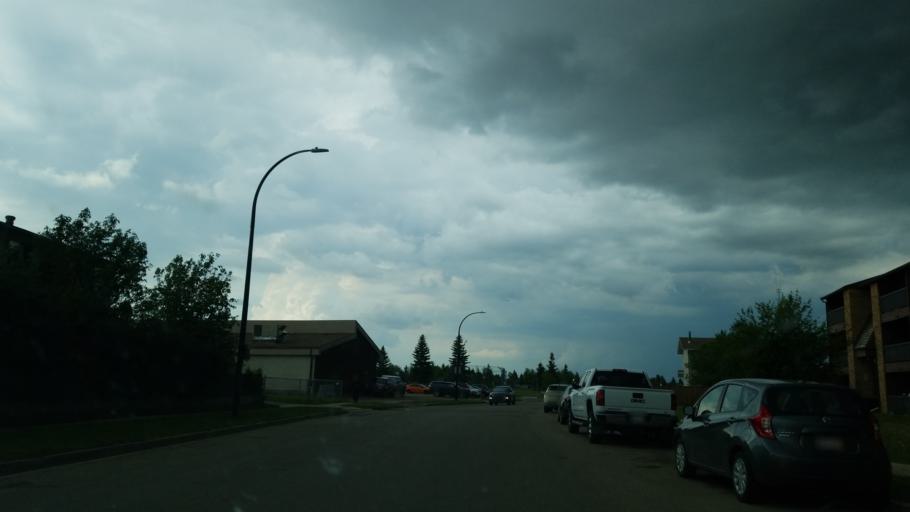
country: CA
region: Saskatchewan
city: Lloydminster
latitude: 53.2660
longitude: -110.0215
